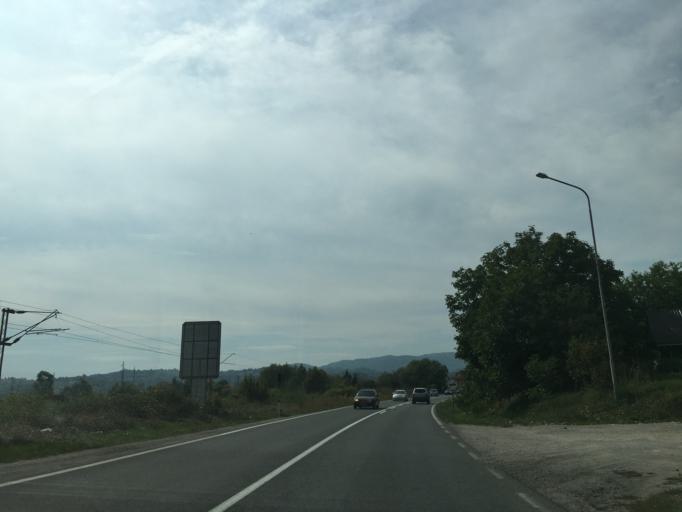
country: RS
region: Central Serbia
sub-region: Zlatiborski Okrug
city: Pozega
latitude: 43.8447
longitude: 20.0623
